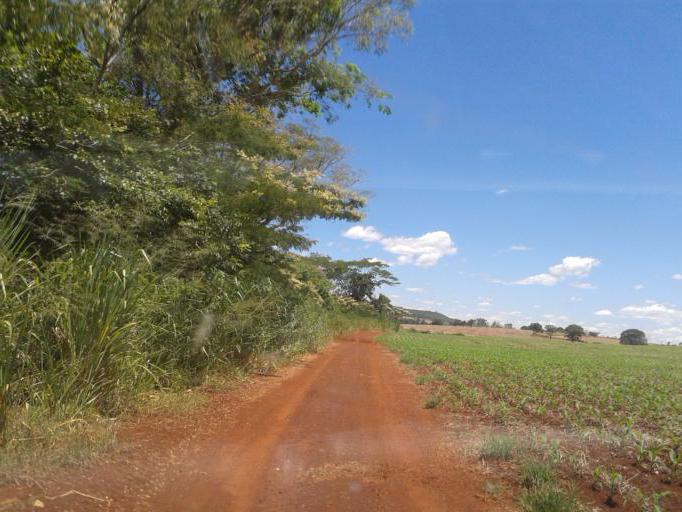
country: BR
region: Minas Gerais
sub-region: Capinopolis
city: Capinopolis
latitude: -18.5850
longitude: -49.5392
